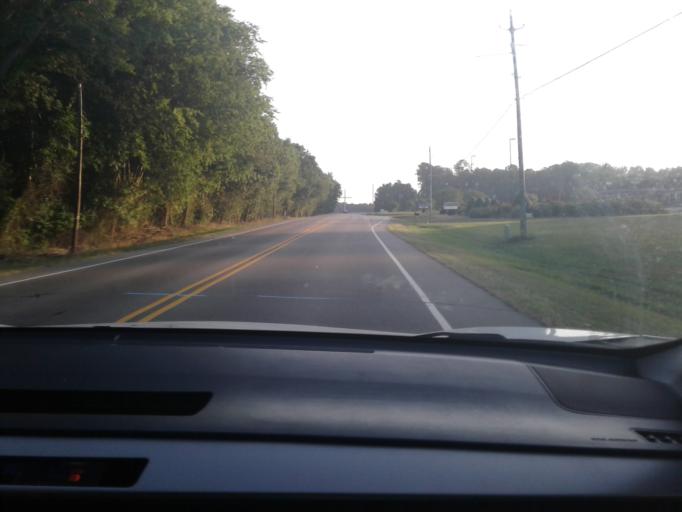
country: US
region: North Carolina
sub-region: Harnett County
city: Lillington
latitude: 35.4711
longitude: -78.8272
